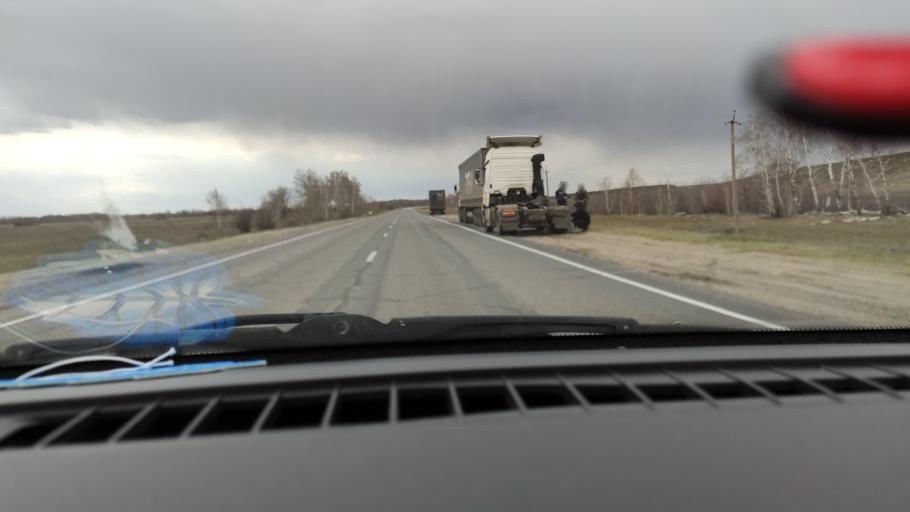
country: RU
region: Saratov
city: Sinodskoye
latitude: 52.0539
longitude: 46.7560
